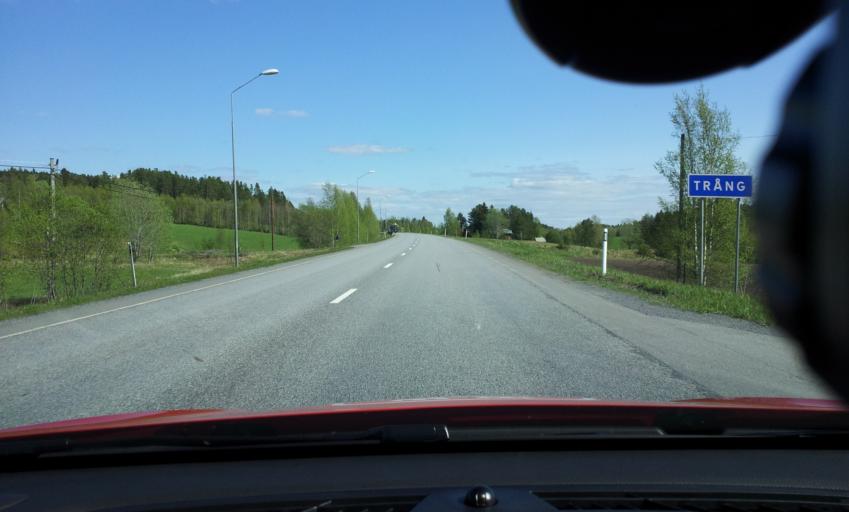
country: SE
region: Jaemtland
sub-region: Krokoms Kommun
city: Valla
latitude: 63.3213
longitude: 14.0637
